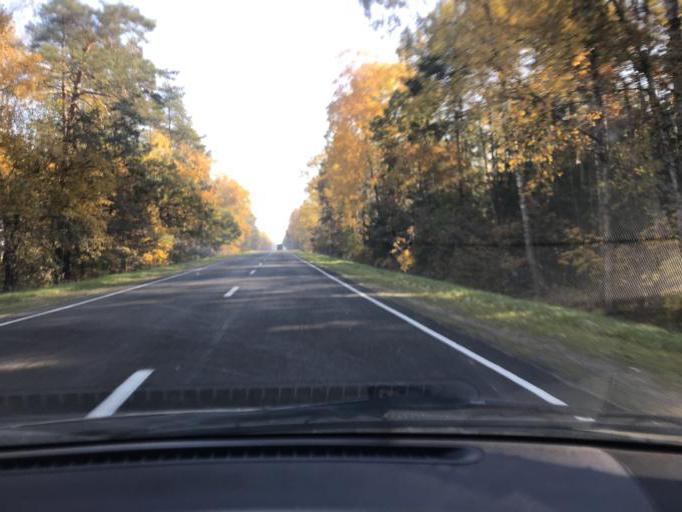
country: BY
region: Brest
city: Lyakhavichy
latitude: 52.9509
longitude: 26.1760
